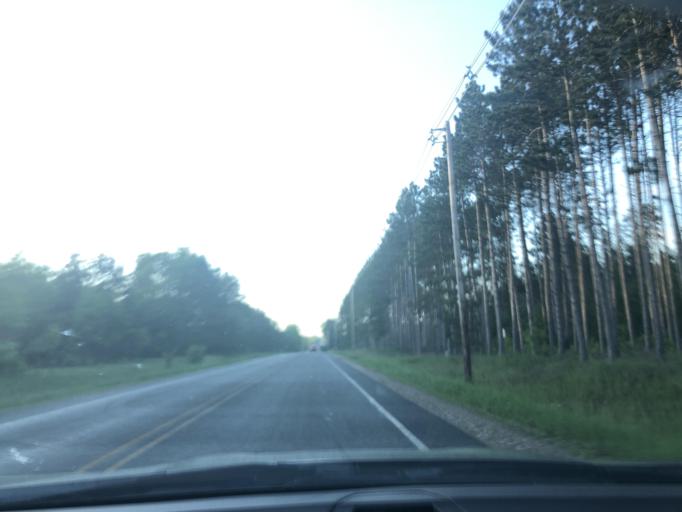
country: US
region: Michigan
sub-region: Missaukee County
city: Lake City
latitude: 44.3597
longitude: -85.0761
